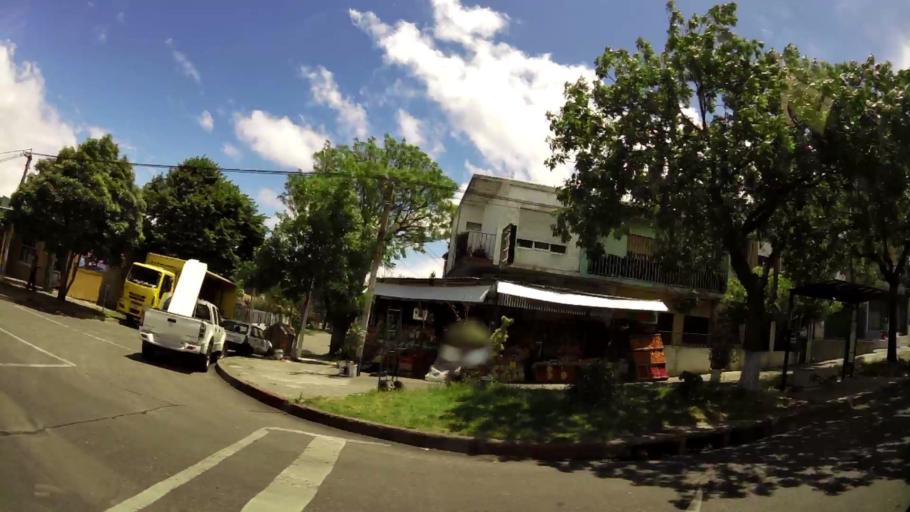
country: UY
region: Montevideo
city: Montevideo
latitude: -34.8576
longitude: -56.1845
